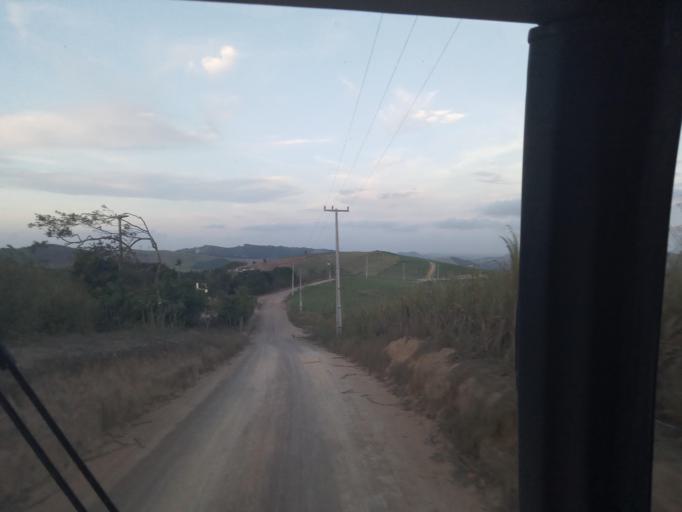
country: BR
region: Pernambuco
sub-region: Vitoria De Santo Antao
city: Vitoria de Santo Antao
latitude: -8.1574
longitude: -35.2535
